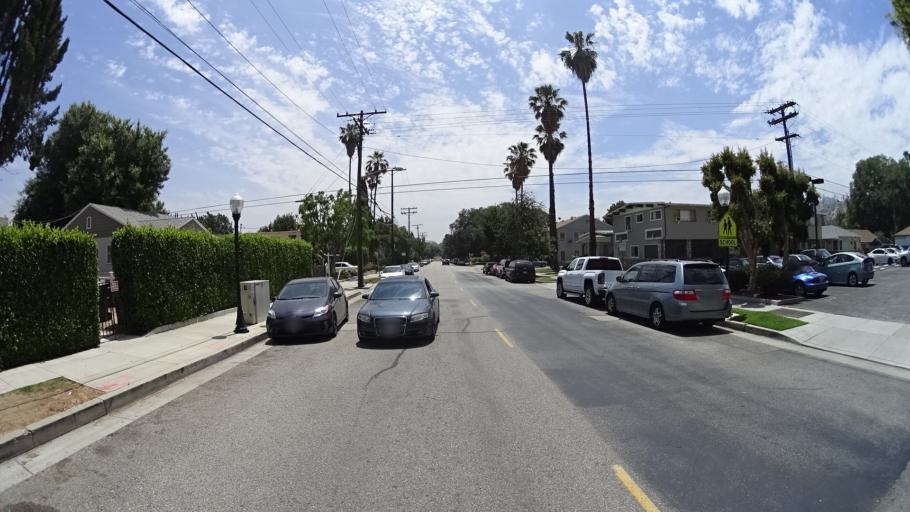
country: US
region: California
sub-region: Los Angeles County
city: Burbank
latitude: 34.1631
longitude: -118.2975
